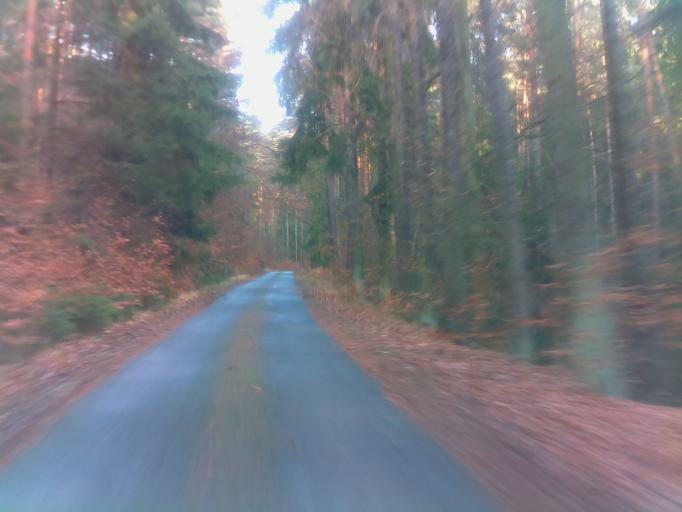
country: DE
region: Thuringia
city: Unterwellenborn
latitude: 50.6880
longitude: 11.4563
